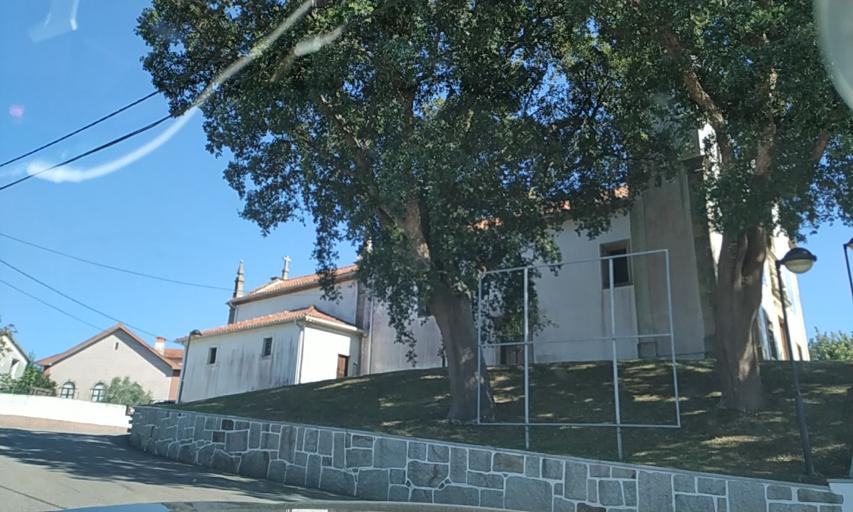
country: PT
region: Aveiro
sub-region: Estarreja
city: Salreu
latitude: 40.7510
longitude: -8.5580
